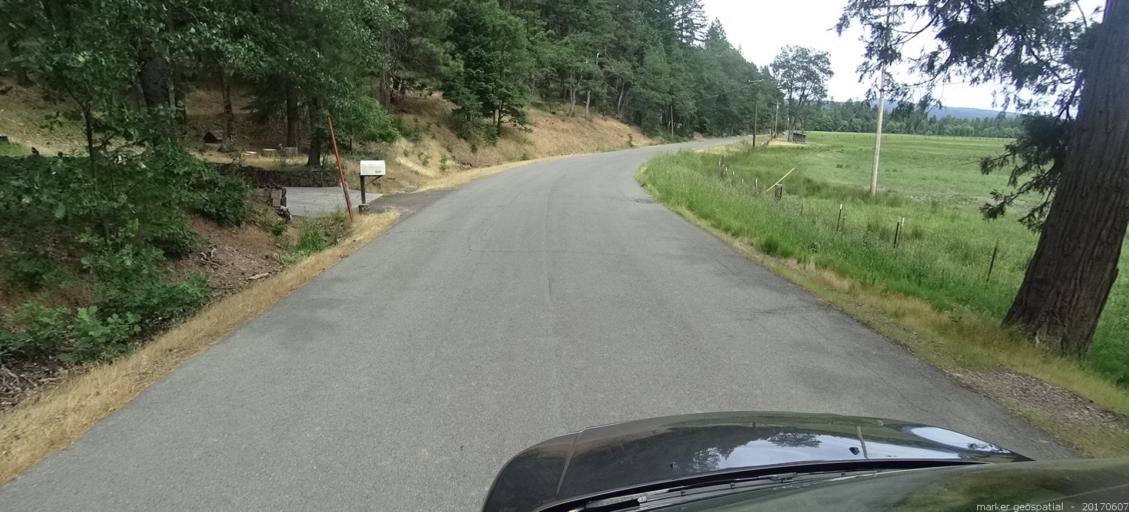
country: US
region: California
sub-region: Siskiyou County
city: Mount Shasta
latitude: 41.3250
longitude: -122.3538
